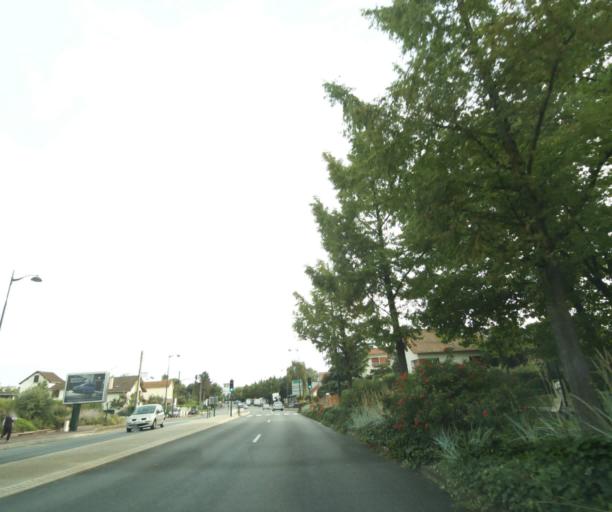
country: FR
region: Ile-de-France
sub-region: Departement des Hauts-de-Seine
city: Le Plessis-Robinson
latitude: 48.7809
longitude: 2.2527
